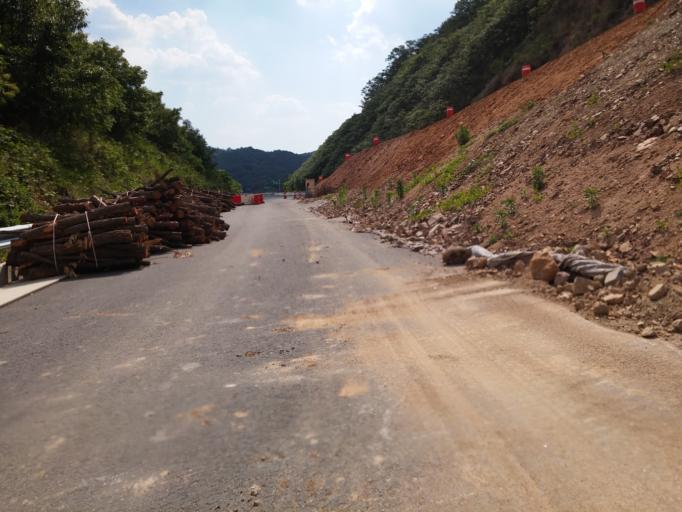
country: KR
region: Daejeon
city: Sintansin
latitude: 36.5043
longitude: 127.4807
